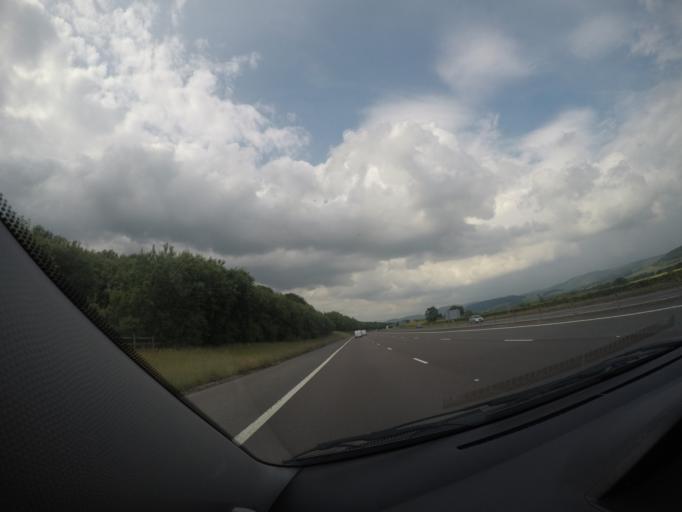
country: GB
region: Scotland
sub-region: Dumfries and Galloway
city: Lochmaben
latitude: 55.2279
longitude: -3.4132
